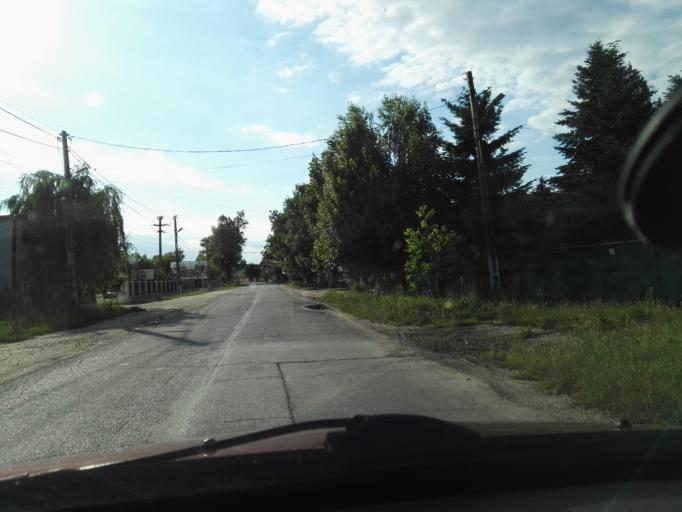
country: RO
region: Ilfov
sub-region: Comuna Copaceni
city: Copaceni
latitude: 44.2428
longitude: 26.1020
